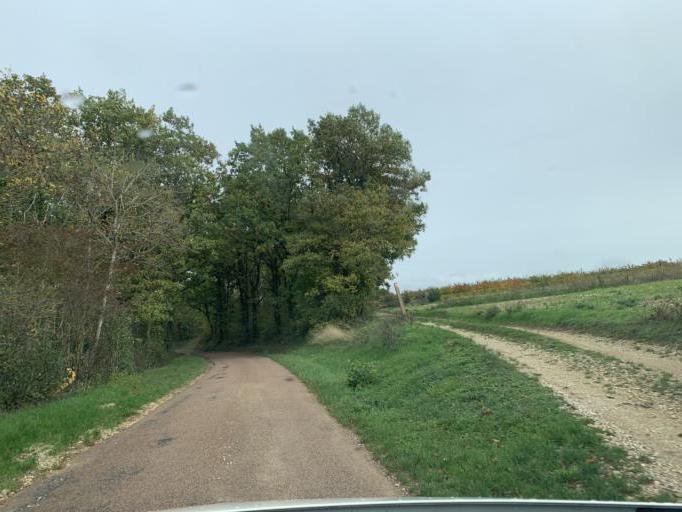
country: FR
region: Bourgogne
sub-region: Departement de l'Yonne
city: Champs-sur-Yonne
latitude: 47.7134
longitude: 3.5705
